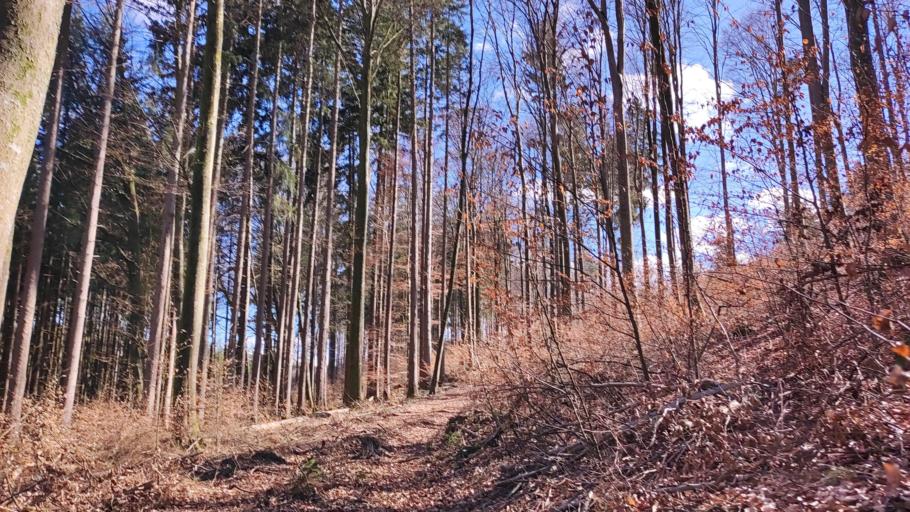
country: DE
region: Bavaria
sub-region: Swabia
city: Zusmarshausen
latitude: 48.4280
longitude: 10.6130
